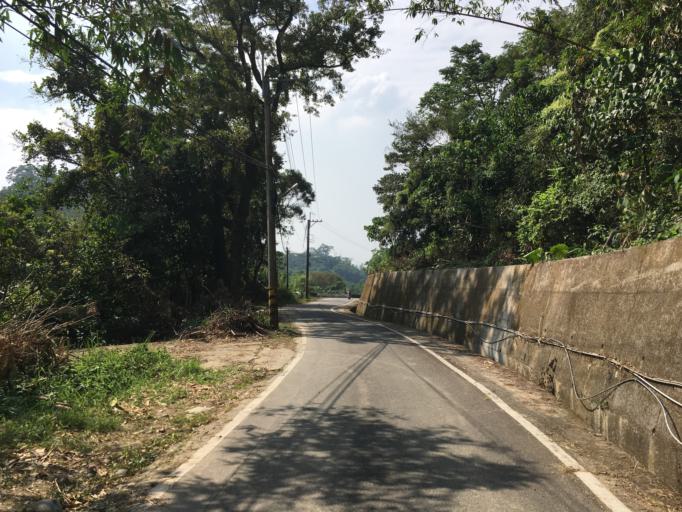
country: TW
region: Taiwan
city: Fengyuan
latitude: 24.1844
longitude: 120.7841
